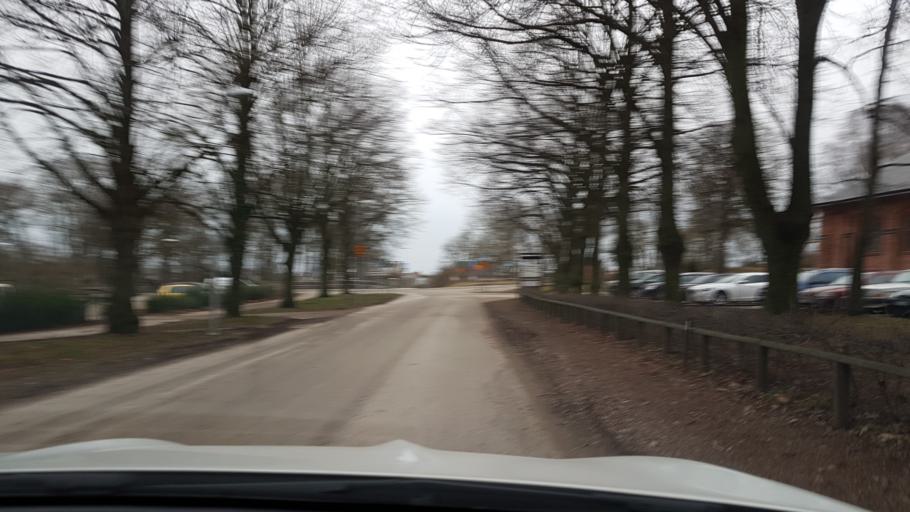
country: SE
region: Gotland
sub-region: Gotland
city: Visby
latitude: 57.6326
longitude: 18.3000
